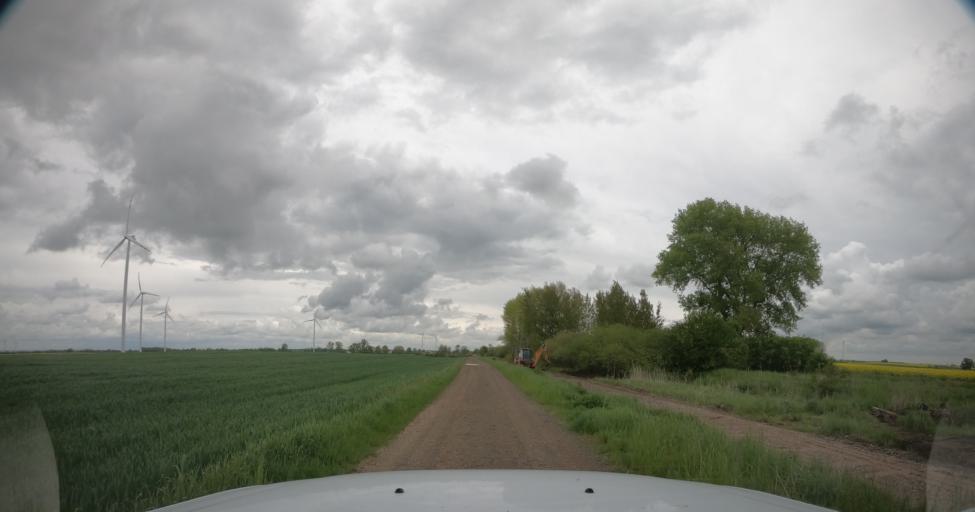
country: PL
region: West Pomeranian Voivodeship
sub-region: Powiat pyrzycki
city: Kozielice
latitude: 53.1036
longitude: 14.8056
